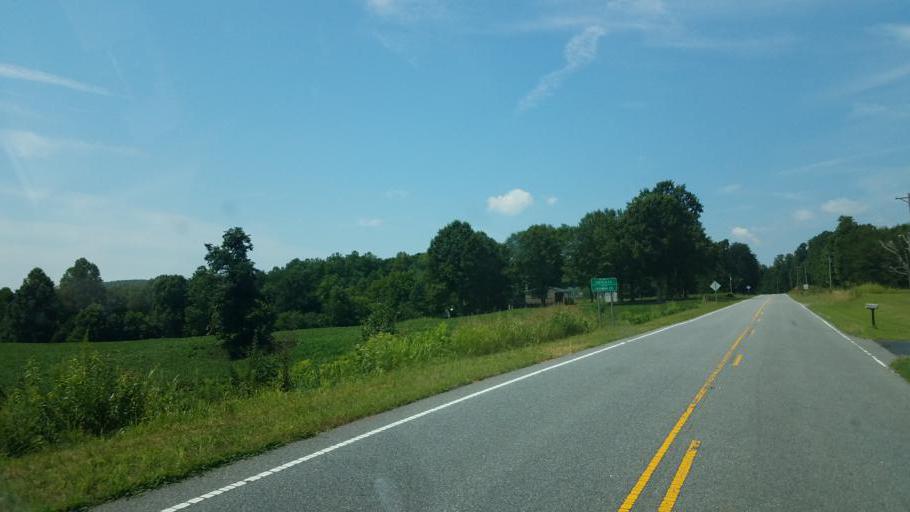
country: US
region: North Carolina
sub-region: Burke County
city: Icard
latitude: 35.5675
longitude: -81.5105
